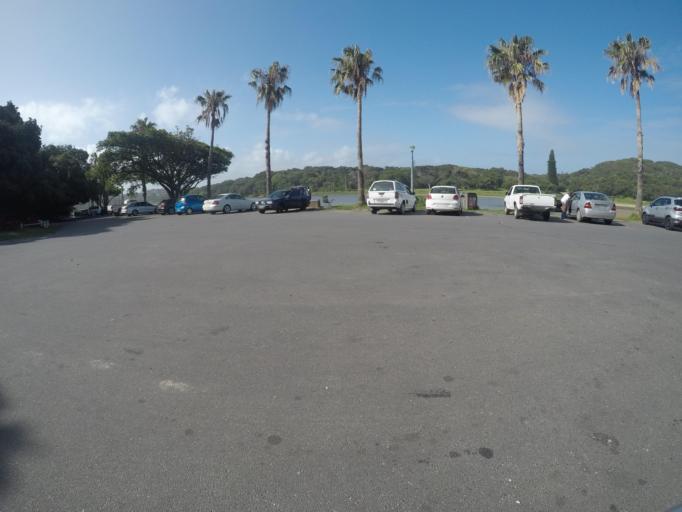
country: ZA
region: Eastern Cape
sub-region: Buffalo City Metropolitan Municipality
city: East London
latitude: -32.9735
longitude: 27.9629
